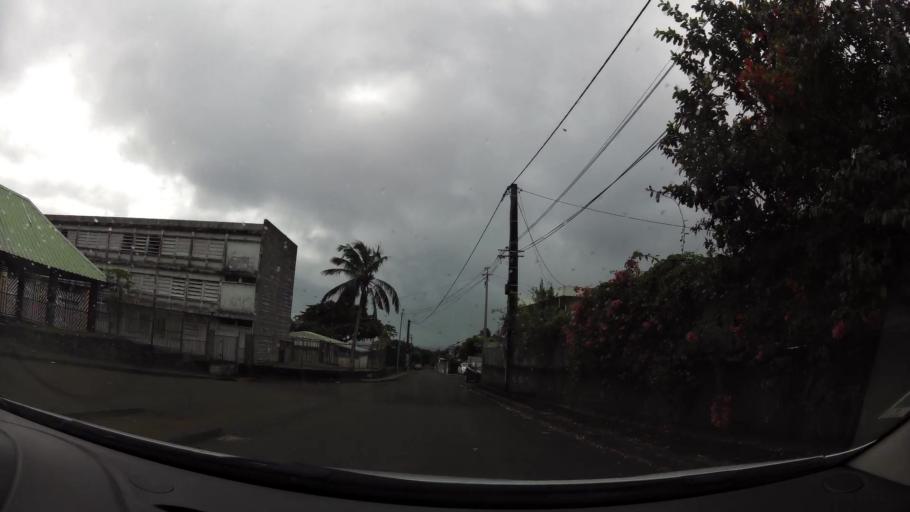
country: RE
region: Reunion
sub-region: Reunion
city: Sainte-Suzanne
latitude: -20.9019
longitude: 55.5994
